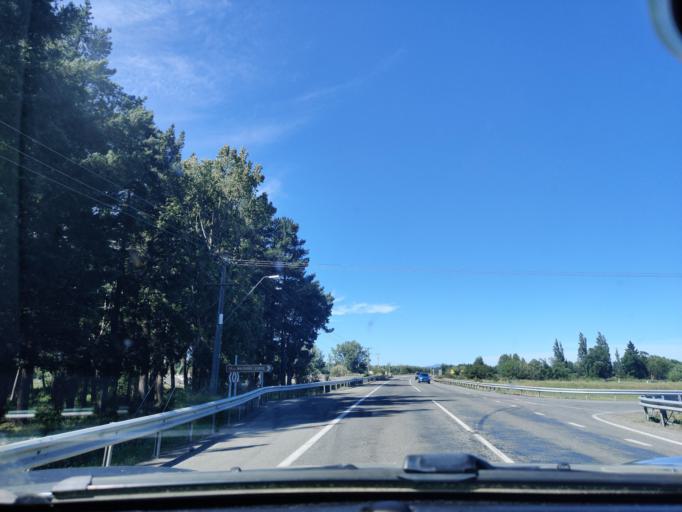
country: NZ
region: Wellington
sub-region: Masterton District
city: Masterton
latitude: -41.0557
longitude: 175.4961
